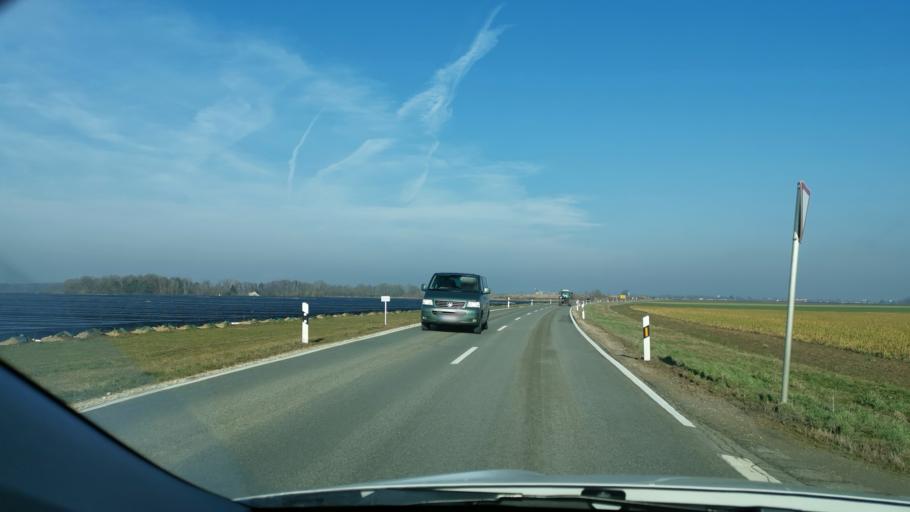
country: DE
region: Bavaria
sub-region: Swabia
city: Munster
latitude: 48.6558
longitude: 10.9210
